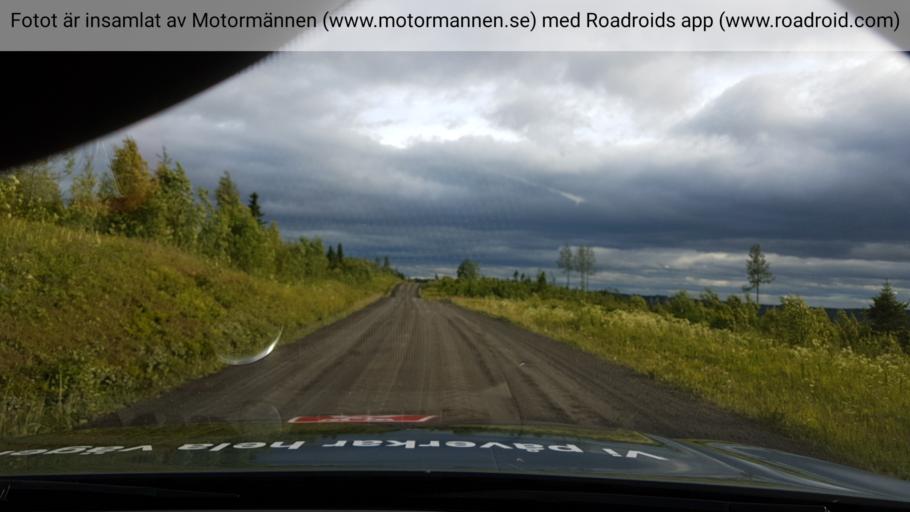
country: SE
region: Jaemtland
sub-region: OEstersunds Kommun
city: Lit
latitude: 63.5972
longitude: 14.9895
